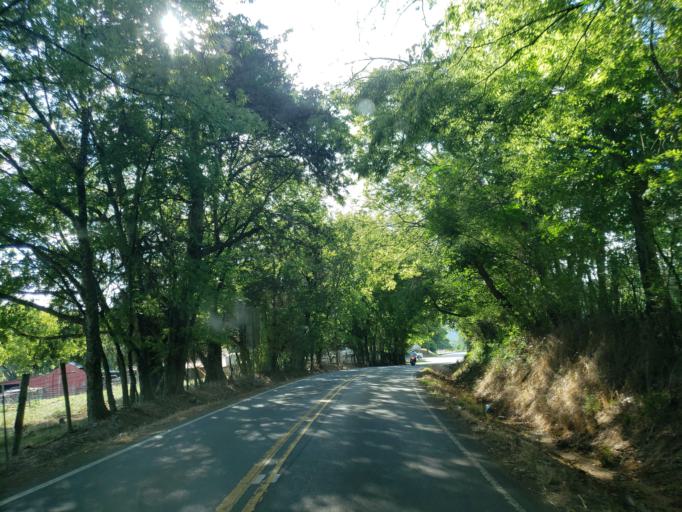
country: US
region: Georgia
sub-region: Floyd County
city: Lindale
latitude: 34.2011
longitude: -85.1127
